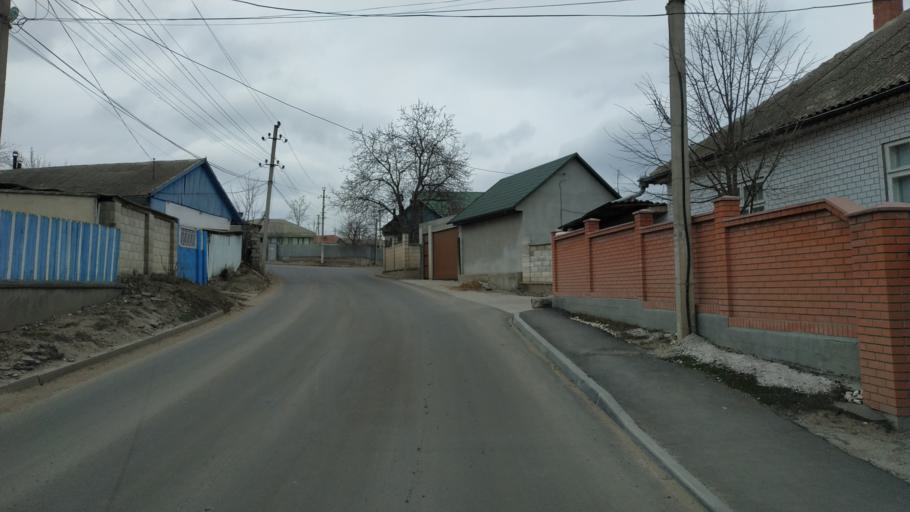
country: MD
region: Laloveni
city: Ialoveni
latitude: 46.8679
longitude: 28.7607
